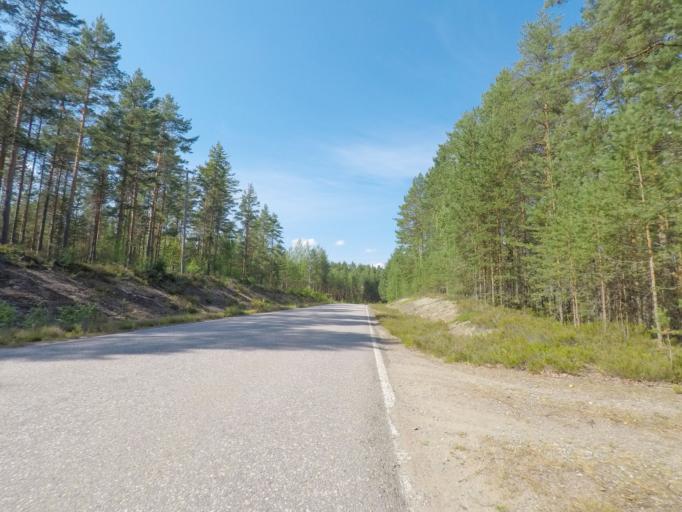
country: FI
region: Southern Savonia
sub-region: Mikkeli
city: Puumala
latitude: 61.4649
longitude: 28.1701
